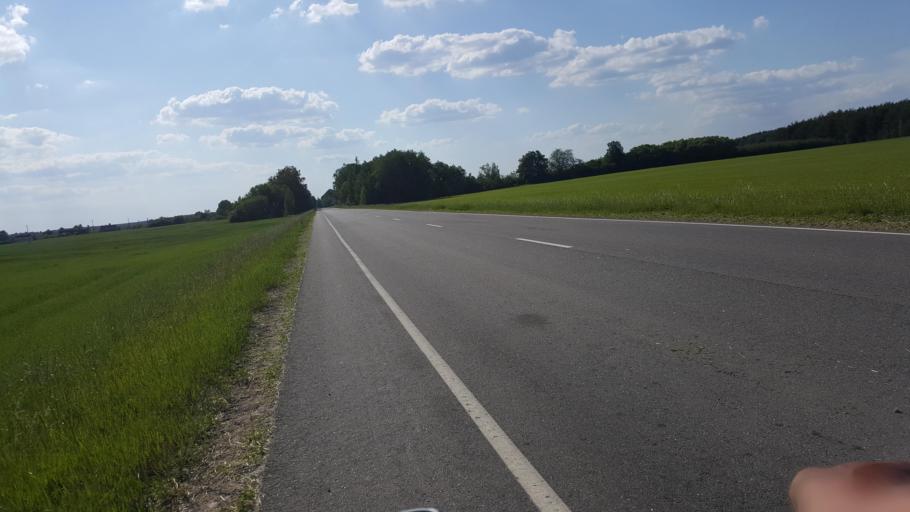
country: BY
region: Brest
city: Zhabinka
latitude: 52.3582
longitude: 24.1651
